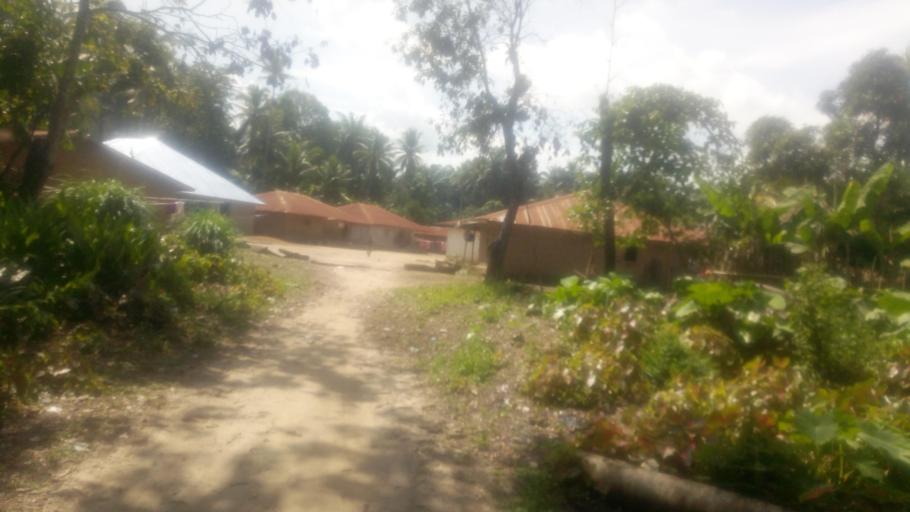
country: SL
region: Northern Province
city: Magburaka
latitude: 8.6623
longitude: -12.0698
